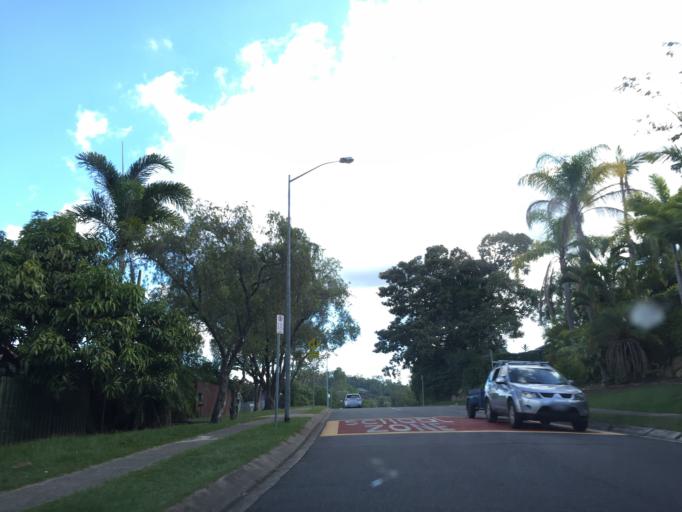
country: AU
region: Queensland
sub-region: Moreton Bay
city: Ferny Hills
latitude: -27.4360
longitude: 152.9385
